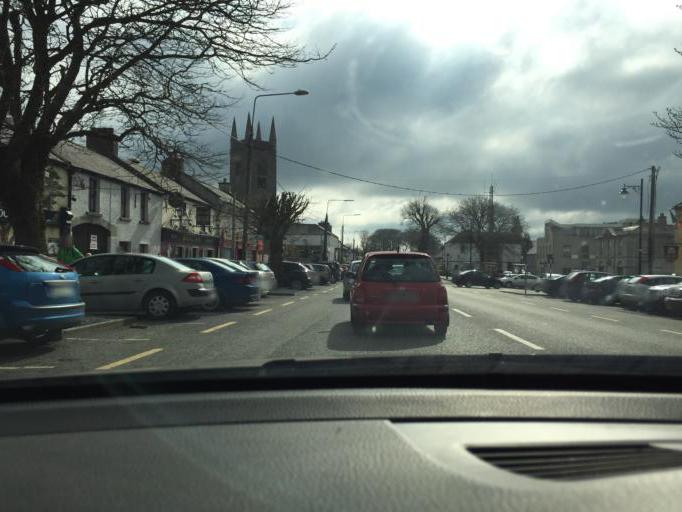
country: IE
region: Leinster
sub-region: Wicklow
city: Blessington
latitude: 53.1716
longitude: -6.5314
